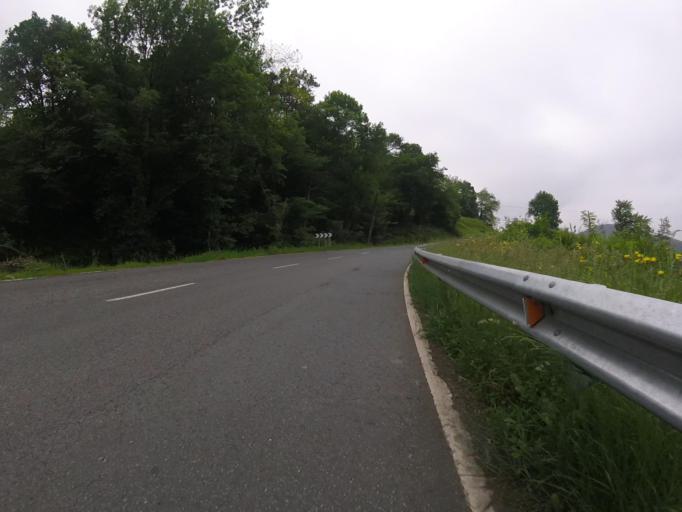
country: ES
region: Navarre
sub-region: Provincia de Navarra
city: Zugarramurdi
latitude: 43.2704
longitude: -1.4940
